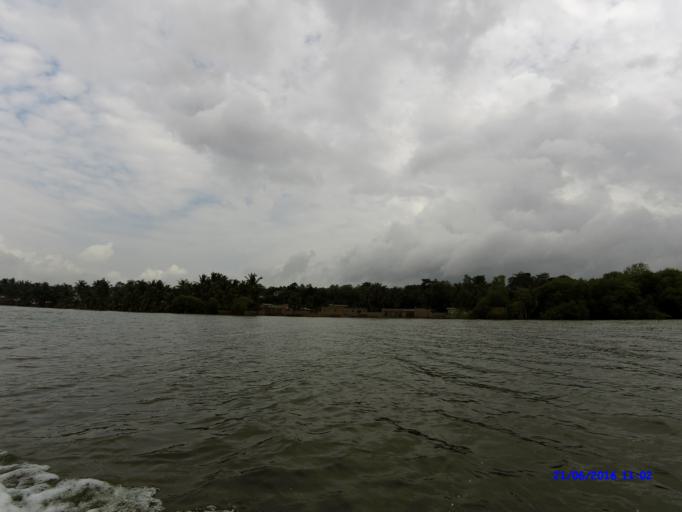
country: BJ
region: Mono
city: Come
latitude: 6.5102
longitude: 1.9671
